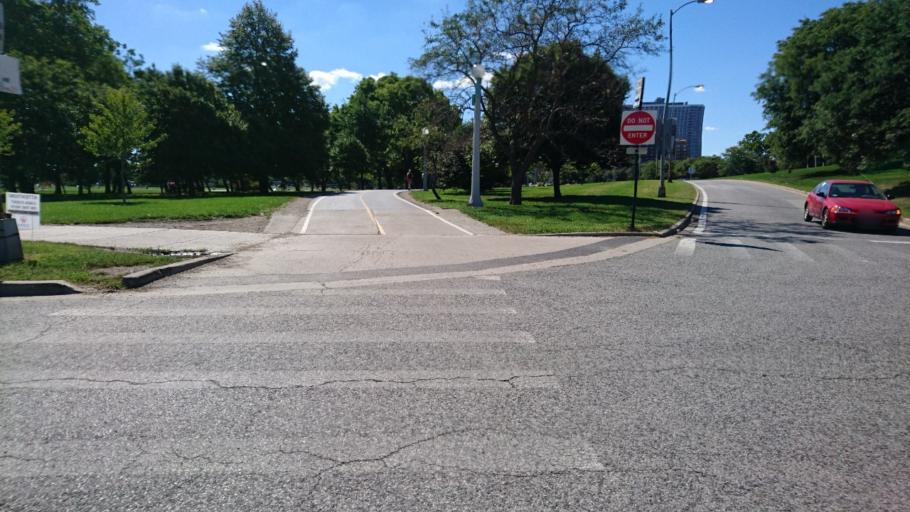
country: US
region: Illinois
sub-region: Cook County
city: Evanston
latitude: 41.9658
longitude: -87.6463
